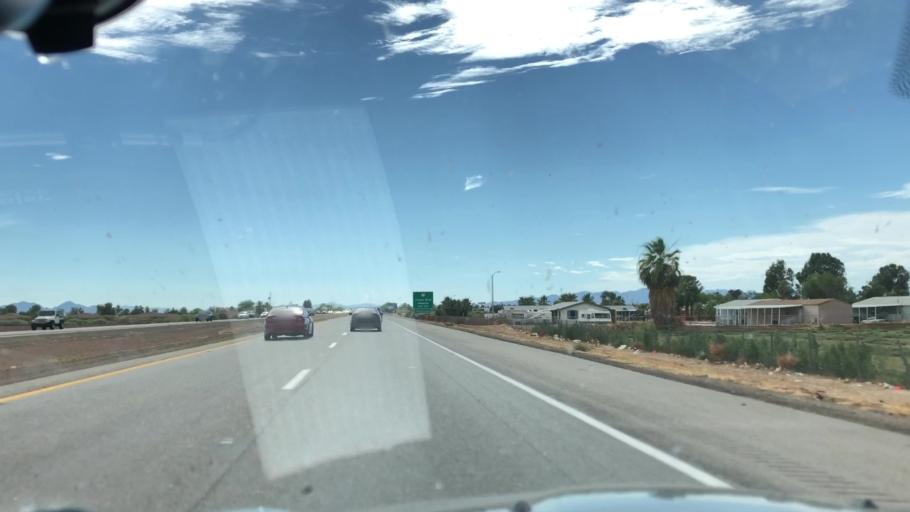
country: US
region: Arizona
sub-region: La Paz County
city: Ehrenberg
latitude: 33.6078
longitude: -114.5566
